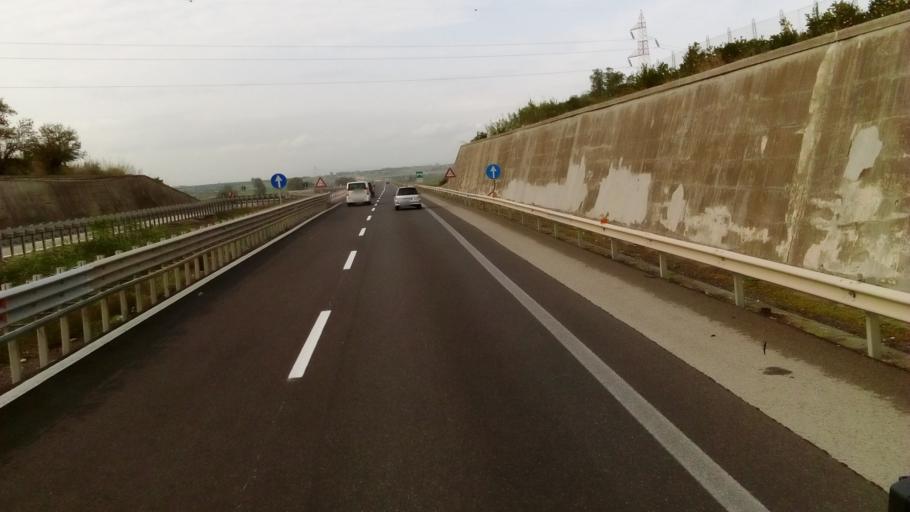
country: IT
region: Sicily
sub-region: Catania
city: Motta Sant'Anastasia
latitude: 37.4684
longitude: 14.9020
